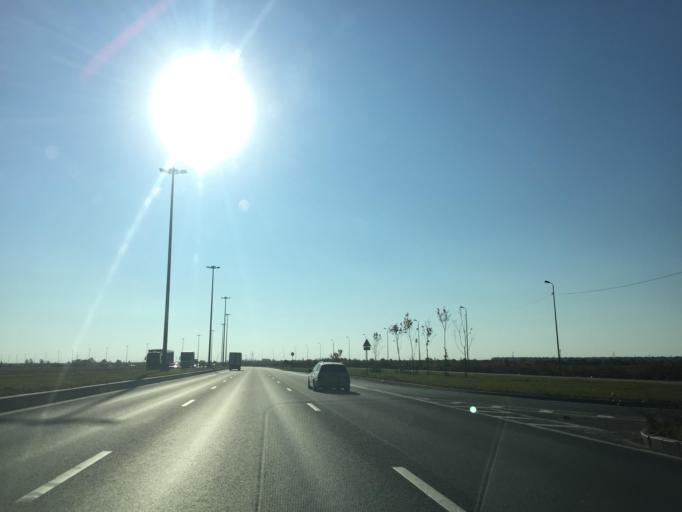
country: RU
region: St.-Petersburg
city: Petro-Slavyanka
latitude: 59.7707
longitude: 30.5000
